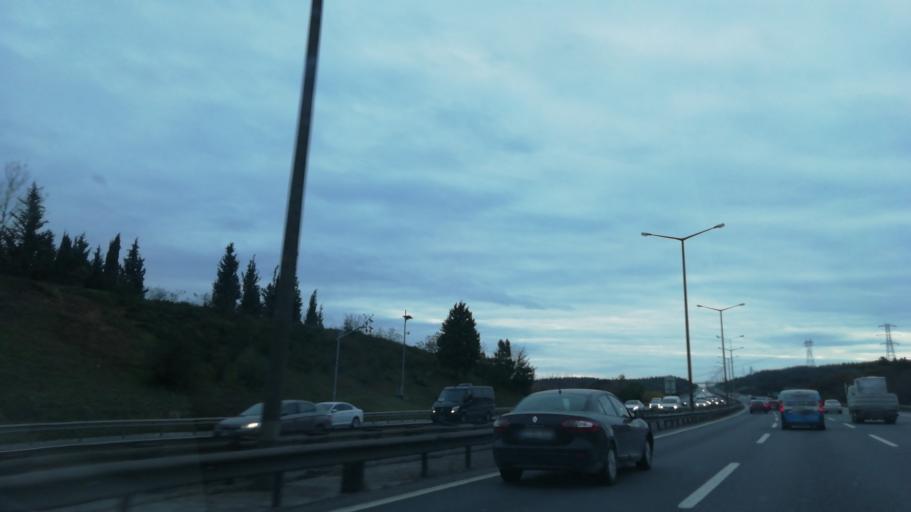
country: TR
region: Istanbul
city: Umraniye
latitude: 41.0791
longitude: 29.0970
